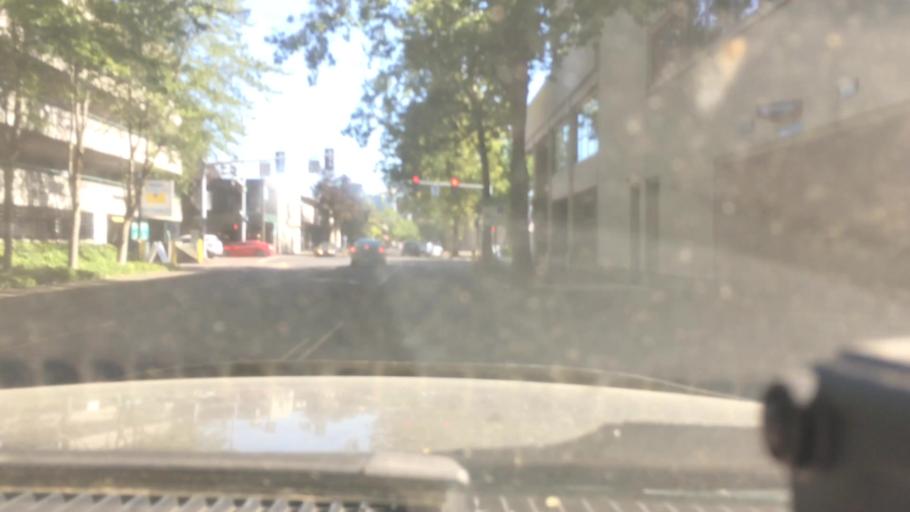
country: US
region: Oregon
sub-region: Lane County
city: Eugene
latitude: 44.0527
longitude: -123.0943
